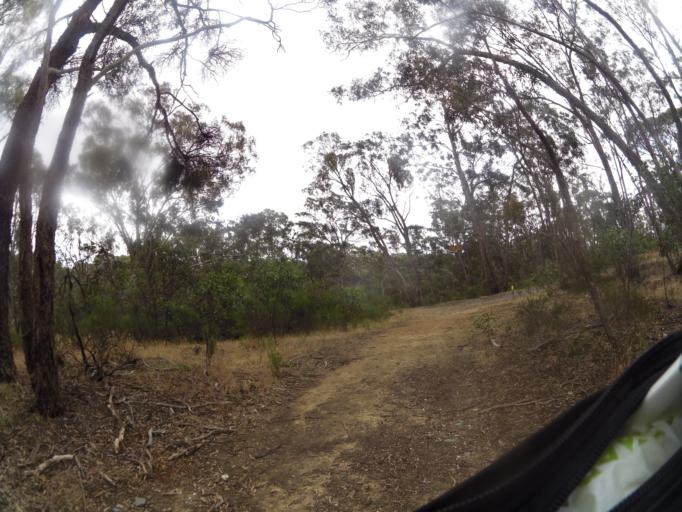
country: AU
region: Victoria
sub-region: Mount Alexander
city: Castlemaine
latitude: -37.0712
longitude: 144.2550
